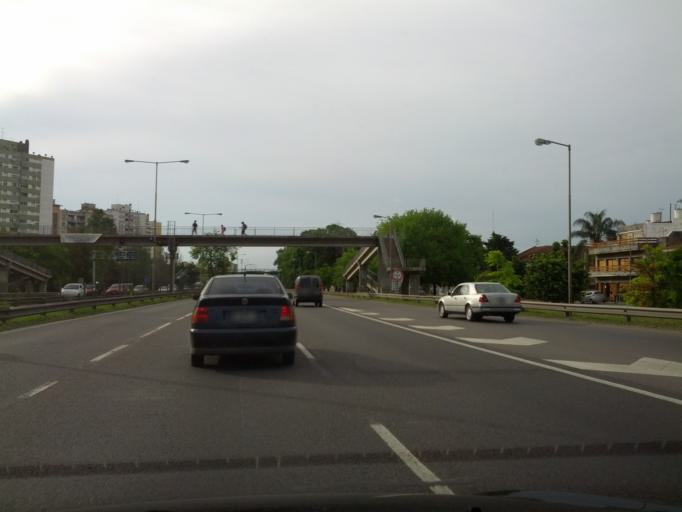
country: AR
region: Buenos Aires F.D.
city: Villa Lugano
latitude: -34.6945
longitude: -58.4749
